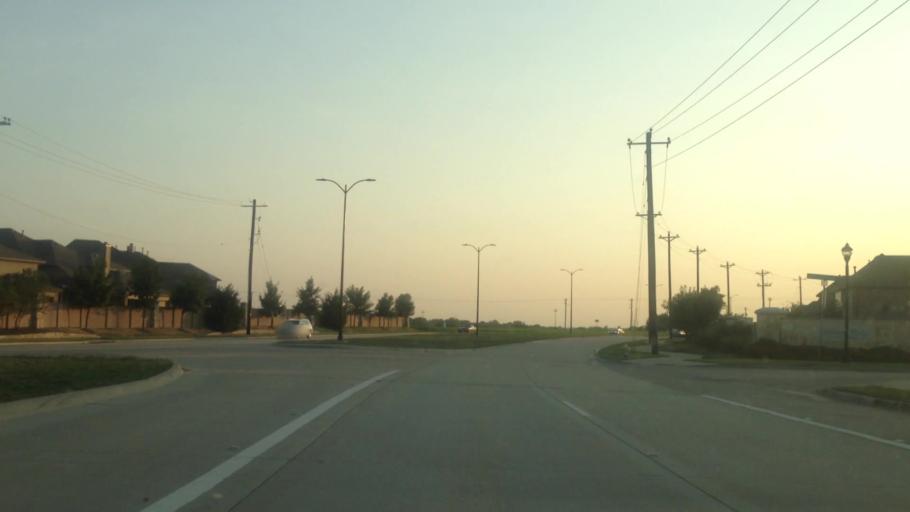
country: US
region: Texas
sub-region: Denton County
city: The Colony
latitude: 33.1149
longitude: -96.8884
